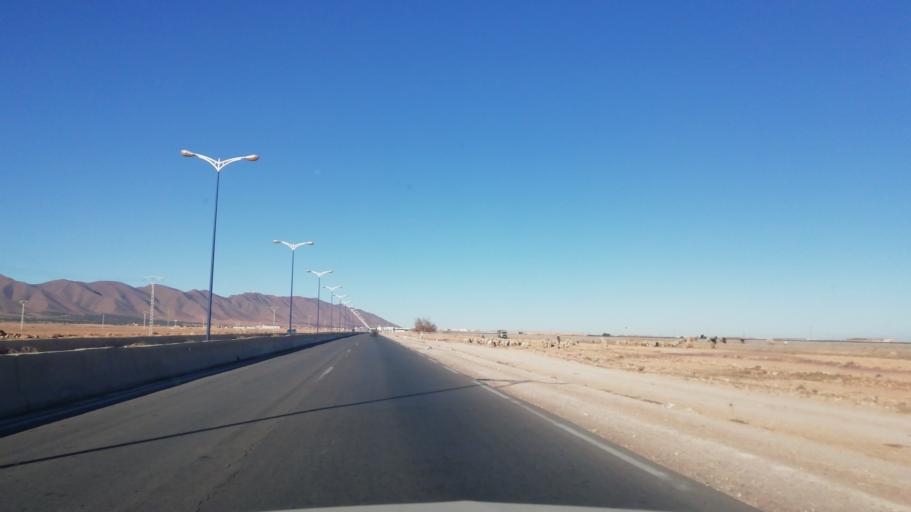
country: DZ
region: Wilaya de Naama
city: Naama
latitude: 33.4928
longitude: -0.2890
